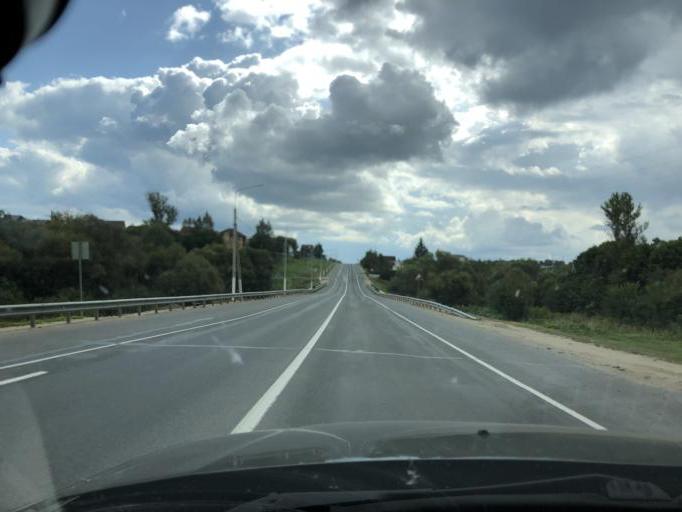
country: RU
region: Tula
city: Gorelki
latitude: 54.3051
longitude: 37.5712
